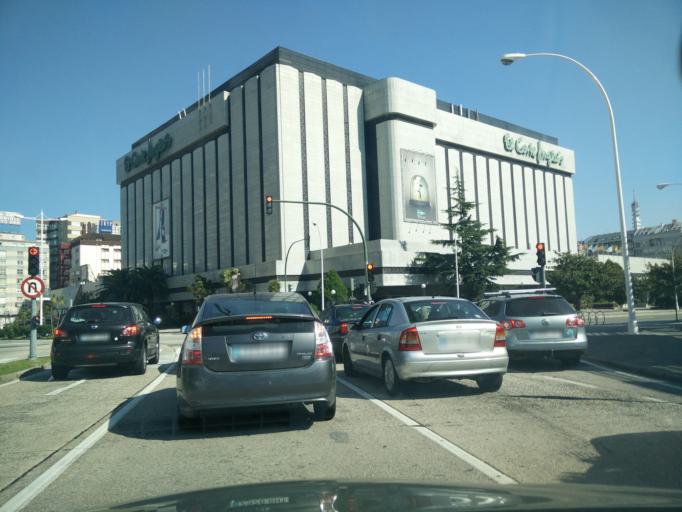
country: ES
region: Galicia
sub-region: Provincia da Coruna
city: A Coruna
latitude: 43.3543
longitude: -8.4044
